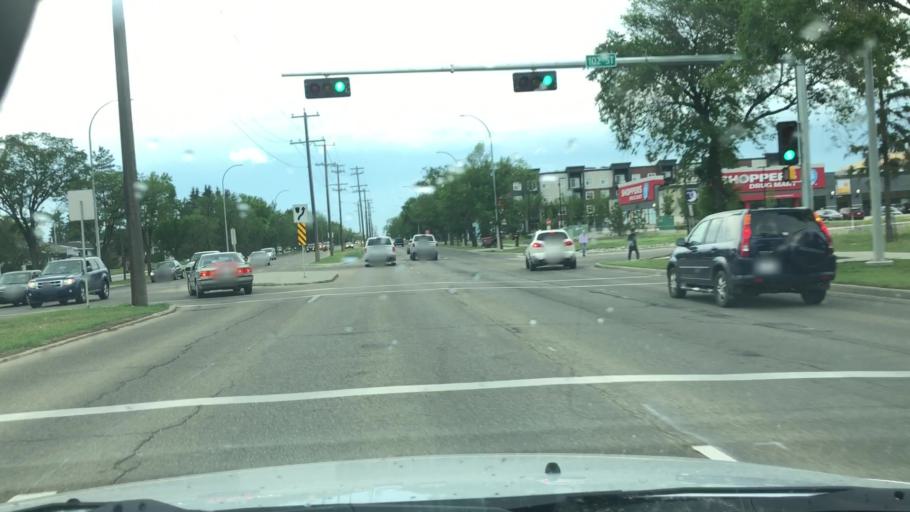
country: CA
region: Alberta
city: Edmonton
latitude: 53.5995
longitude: -113.4950
